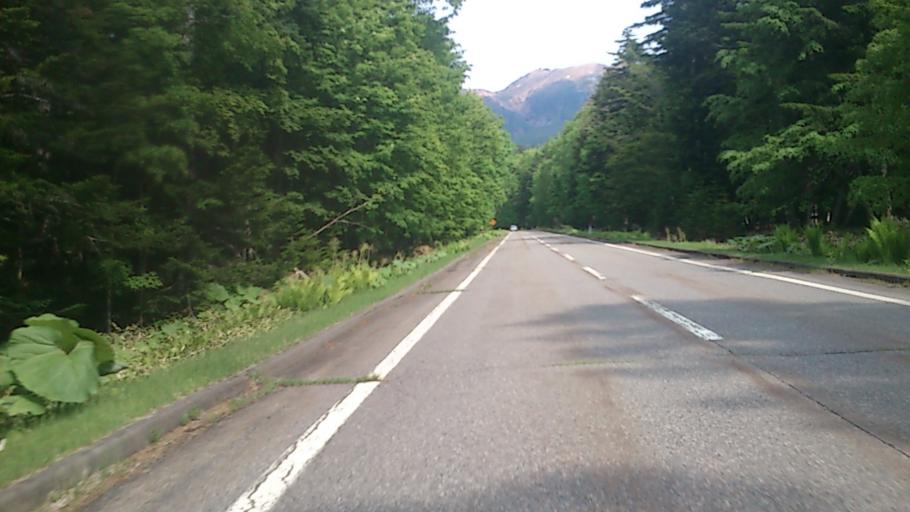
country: JP
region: Hokkaido
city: Kitami
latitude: 43.4035
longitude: 143.9641
